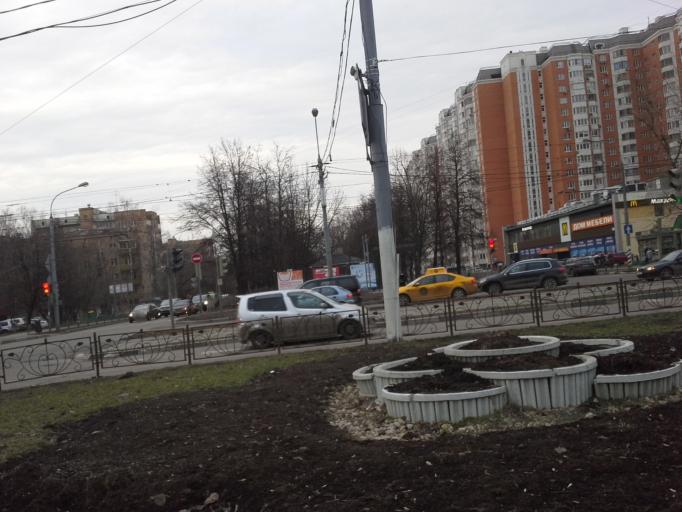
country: RU
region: Moscow
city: Kotlovka
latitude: 55.6532
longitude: 37.6050
